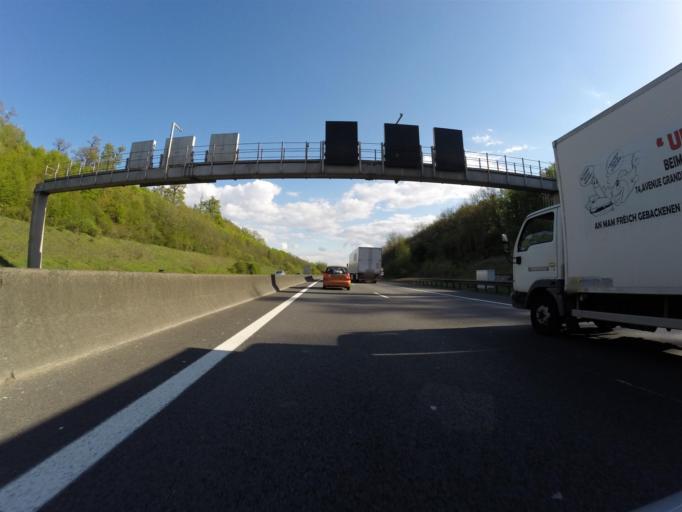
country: LU
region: Luxembourg
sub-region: Canton de Luxembourg
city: Hesperange
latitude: 49.5636
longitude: 6.1293
